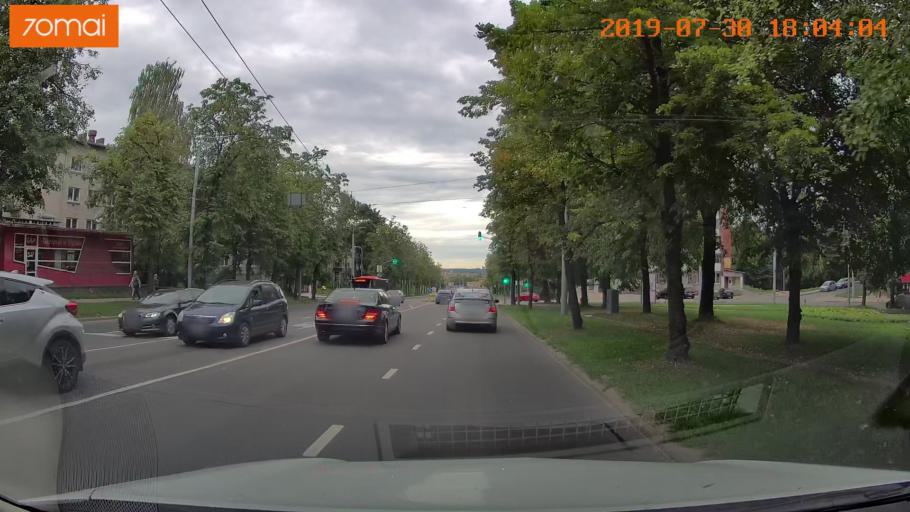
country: LT
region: Vilnius County
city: Naujamiestis
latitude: 54.6624
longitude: 25.2736
